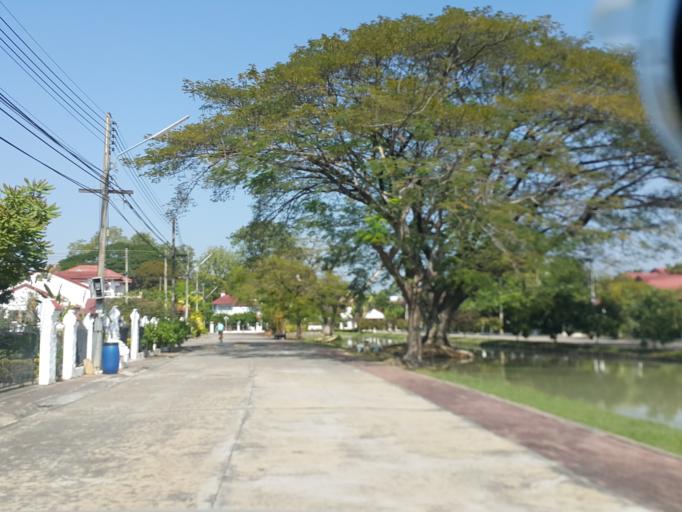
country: TH
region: Chiang Mai
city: Saraphi
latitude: 18.7585
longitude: 99.0250
